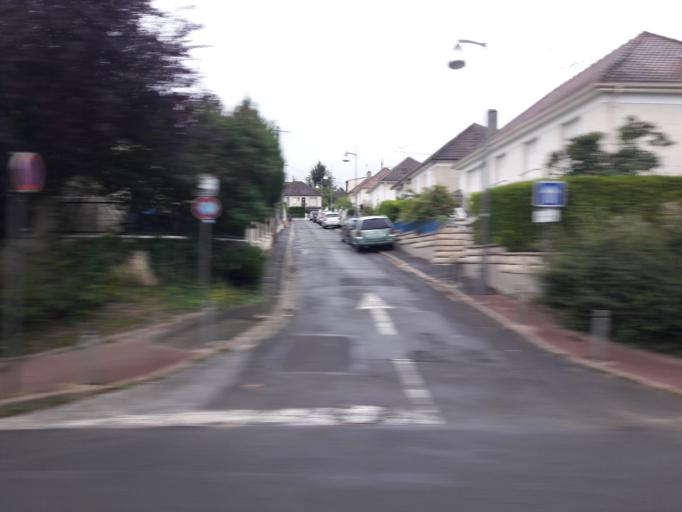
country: FR
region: Ile-de-France
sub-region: Departement de l'Essonne
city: Longjumeau
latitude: 48.6909
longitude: 2.2991
